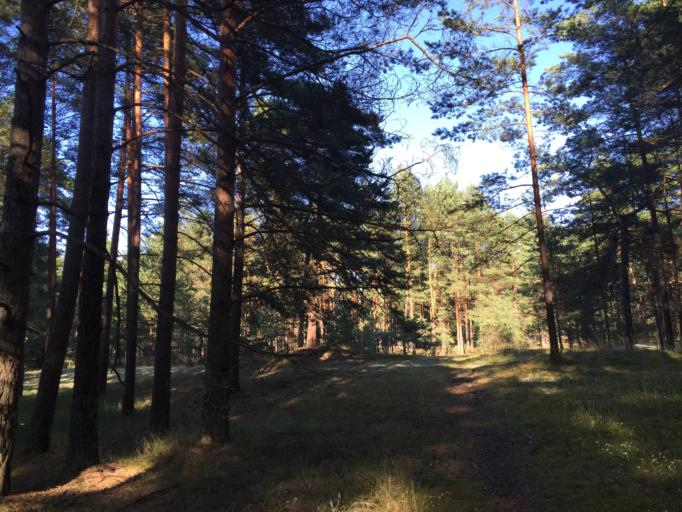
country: LV
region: Riga
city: Jaunciems
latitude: 57.0688
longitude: 24.1337
